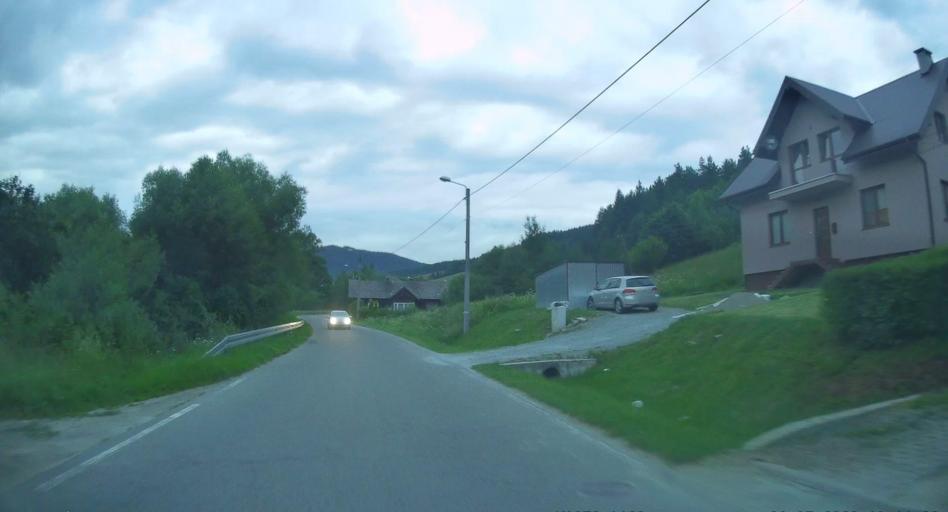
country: PL
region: Lesser Poland Voivodeship
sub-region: Powiat nowosadecki
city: Muszyna
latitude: 49.3794
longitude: 20.9232
